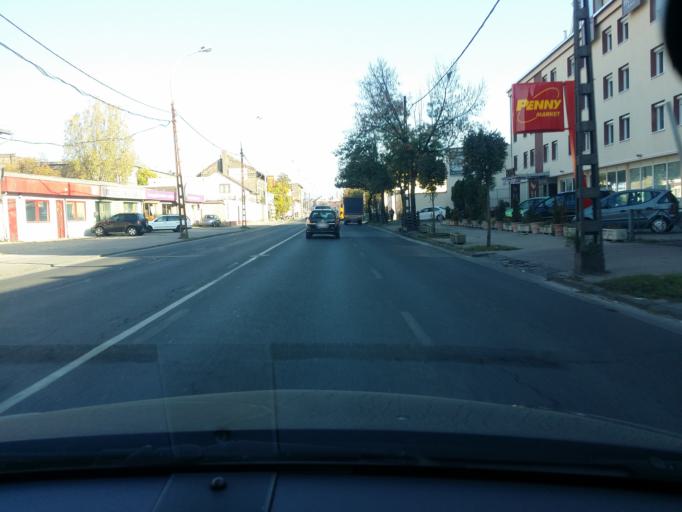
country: HU
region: Budapest
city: Budapest IV. keruelet
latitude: 47.5662
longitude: 19.0796
